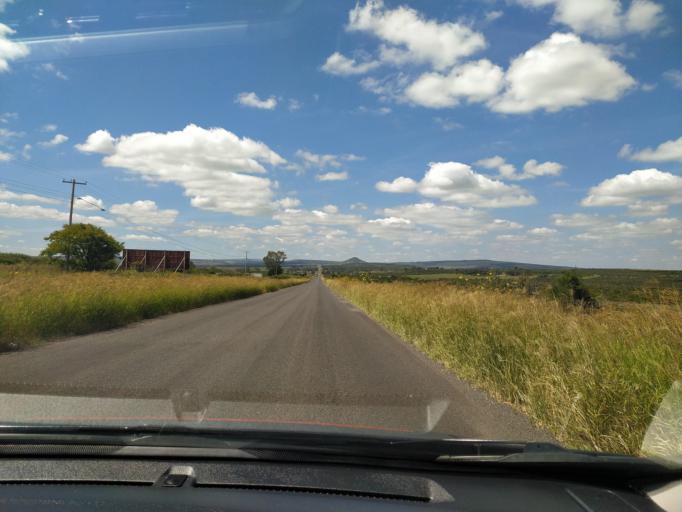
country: MX
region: Jalisco
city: San Diego de Alejandria
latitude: 21.0081
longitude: -102.0181
